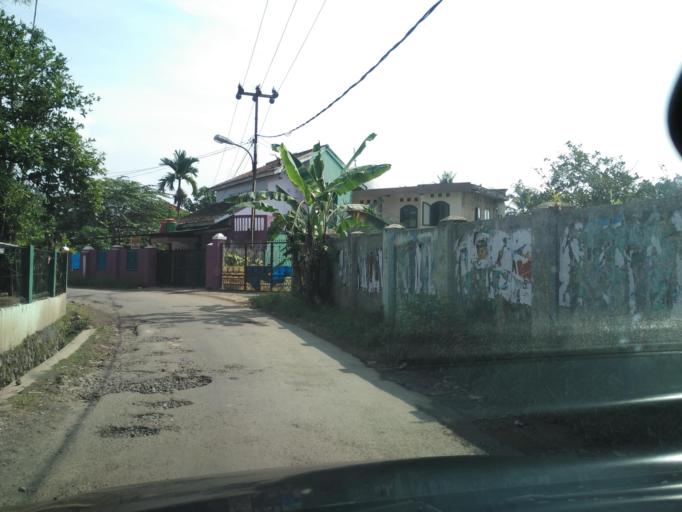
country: ID
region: West Java
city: Ciranjang-hilir
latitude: -6.8036
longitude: 107.1692
